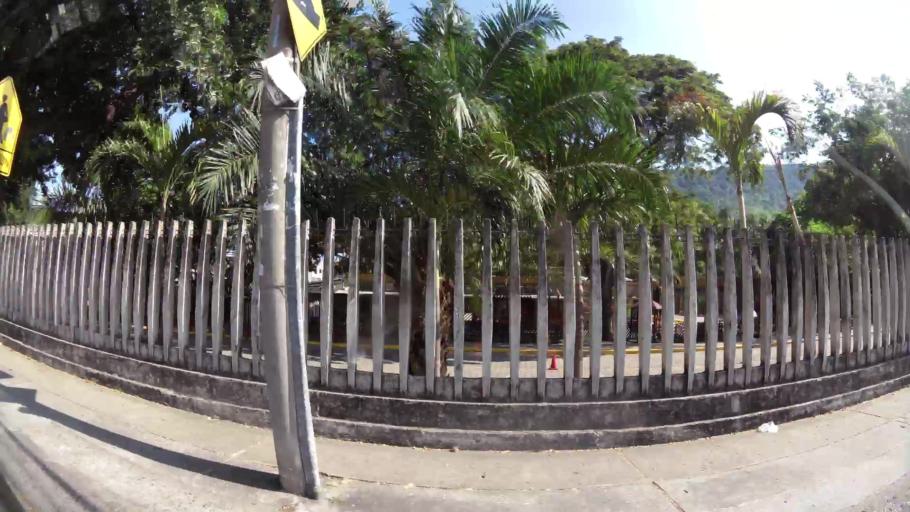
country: EC
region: Guayas
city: Guayaquil
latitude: -2.1666
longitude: -79.9422
